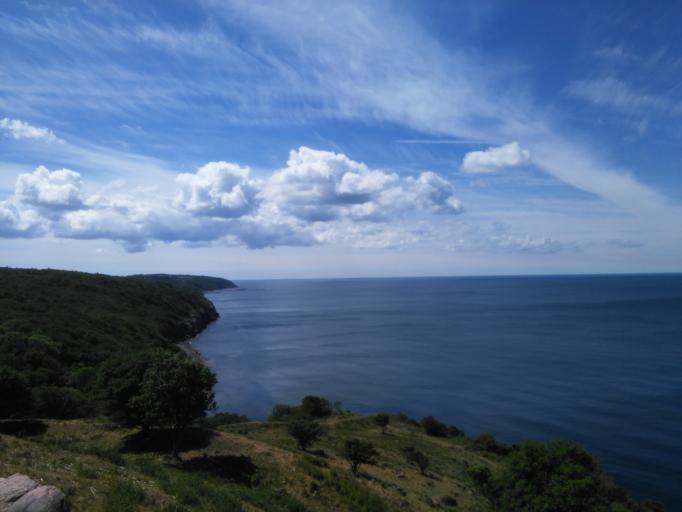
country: DK
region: Capital Region
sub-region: Bornholm Kommune
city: Ronne
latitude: 55.2706
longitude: 14.7543
